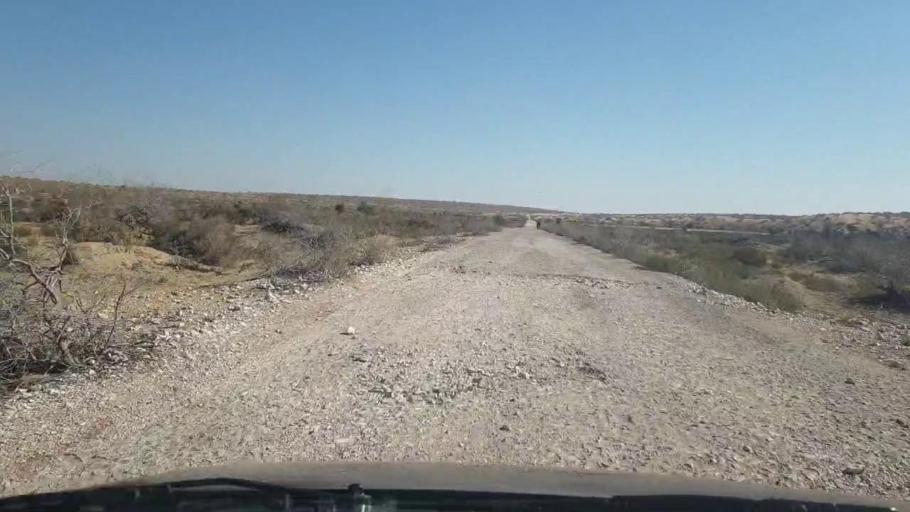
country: PK
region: Sindh
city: Bozdar
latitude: 27.0213
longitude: 68.7204
